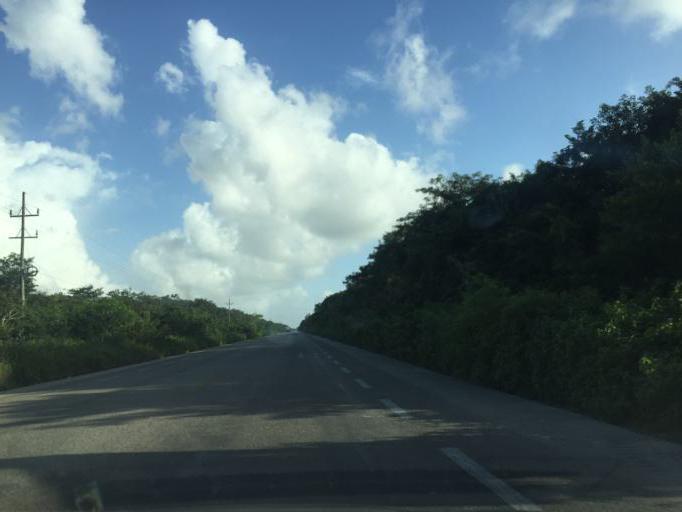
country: MX
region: Quintana Roo
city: Coba
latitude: 20.4791
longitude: -87.6939
